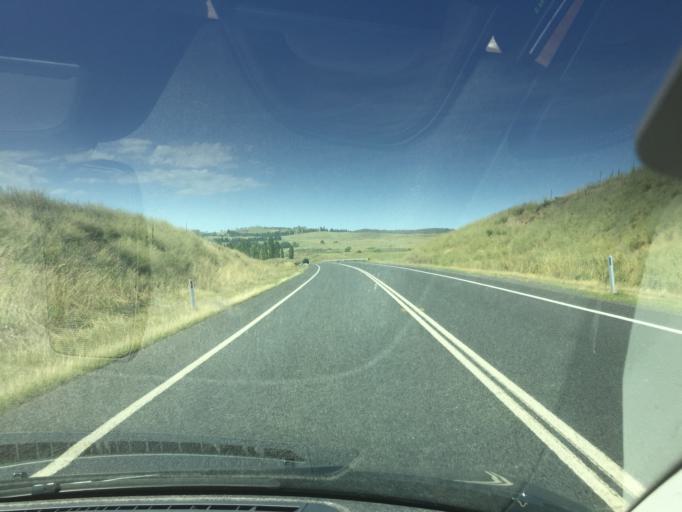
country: AU
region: New South Wales
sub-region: Cooma-Monaro
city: Cooma
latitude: -36.0781
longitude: 149.1596
